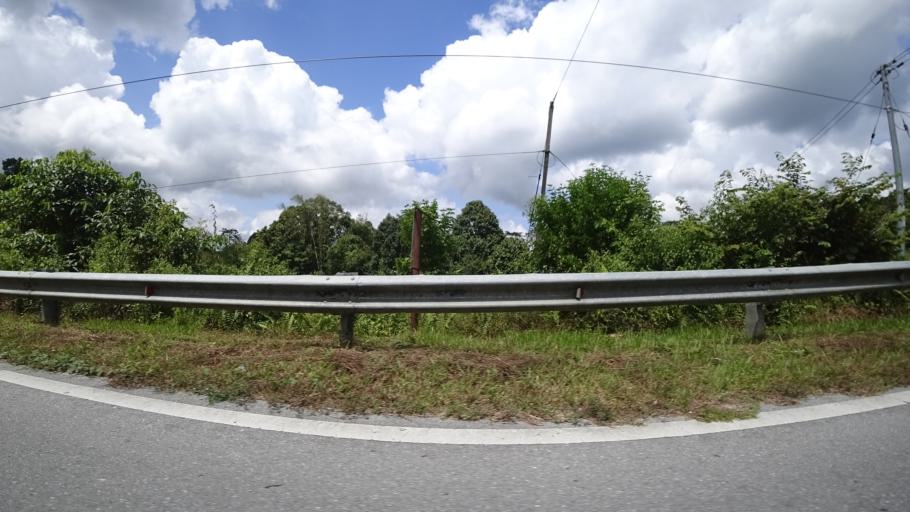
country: BN
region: Tutong
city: Tutong
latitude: 4.7119
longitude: 114.7959
